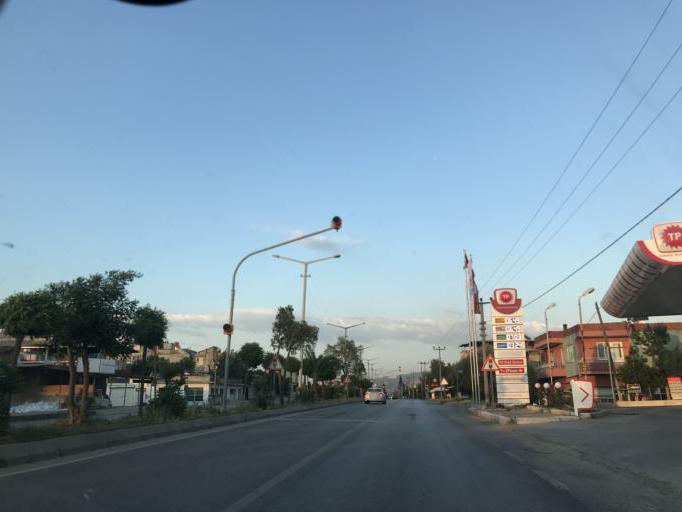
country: TR
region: Aydin
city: Horsunlu
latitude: 37.9131
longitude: 28.5907
